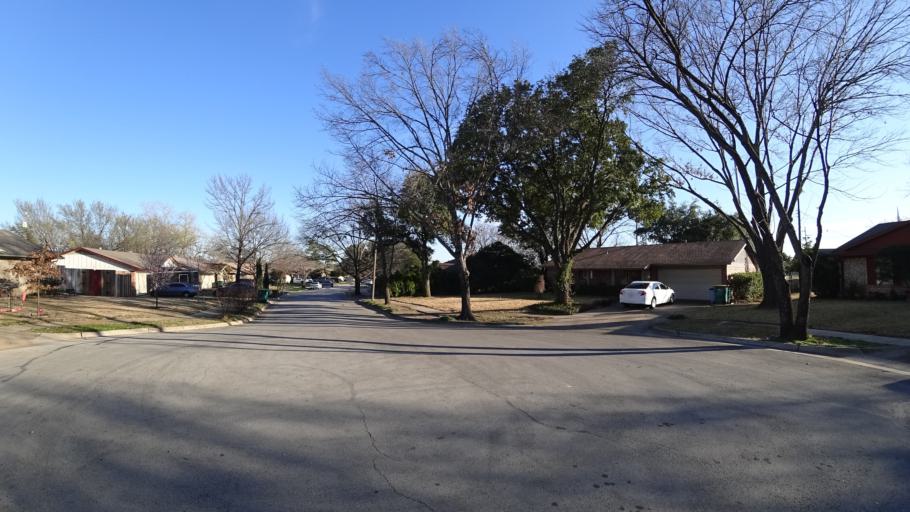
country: US
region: Texas
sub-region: Denton County
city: Lewisville
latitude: 33.0363
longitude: -97.0088
